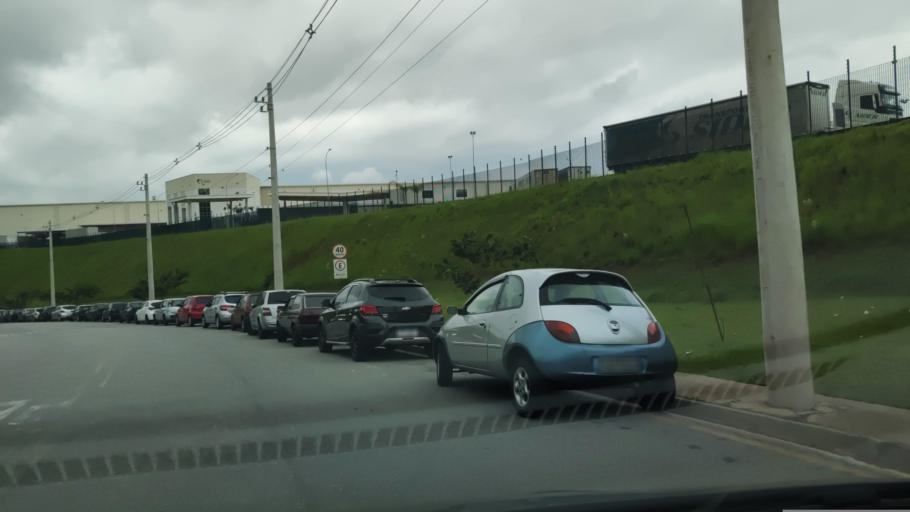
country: BR
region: Sao Paulo
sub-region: Cajamar
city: Cajamar
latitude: -23.3338
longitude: -46.8500
